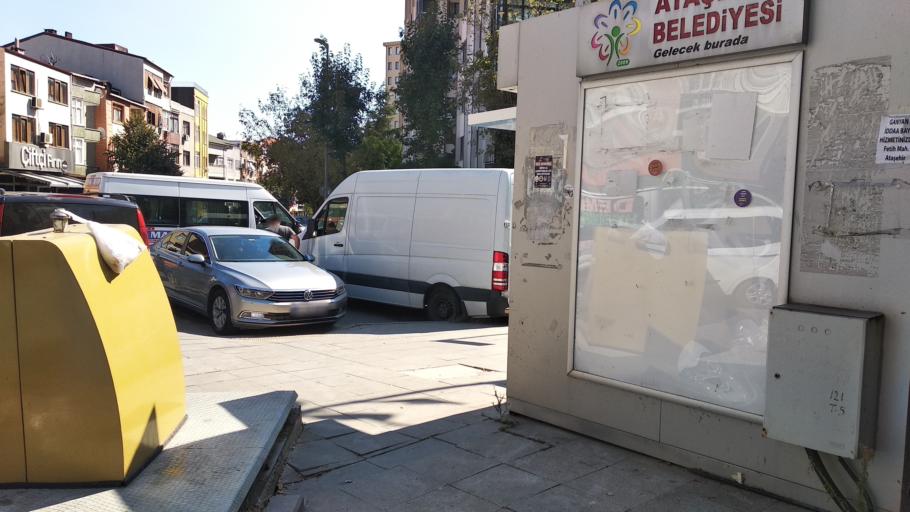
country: TR
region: Istanbul
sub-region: Atasehir
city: Atasehir
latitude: 41.0033
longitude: 29.0743
